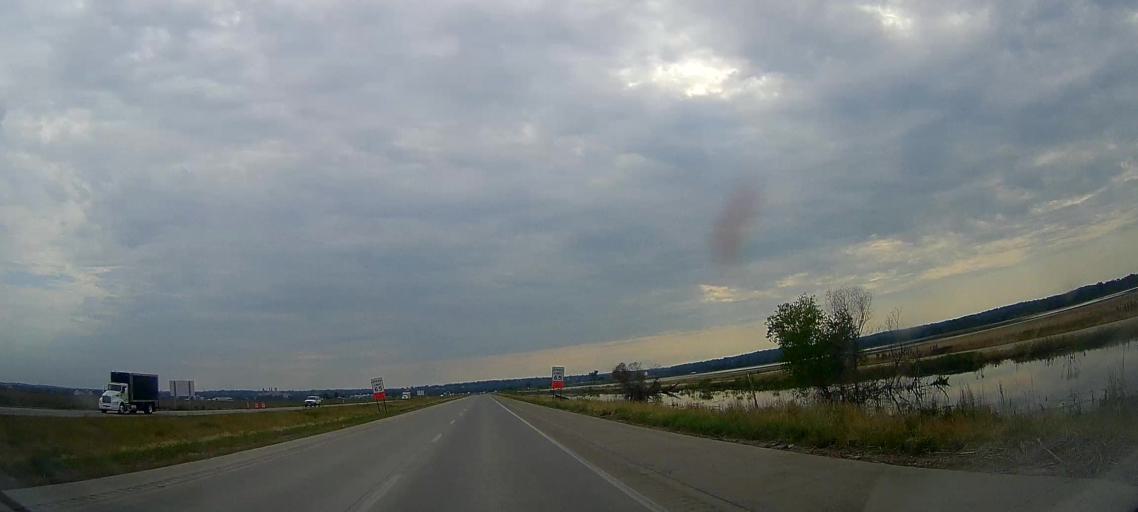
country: US
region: Iowa
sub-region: Pottawattamie County
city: Carter Lake
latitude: 41.3504
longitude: -95.9141
